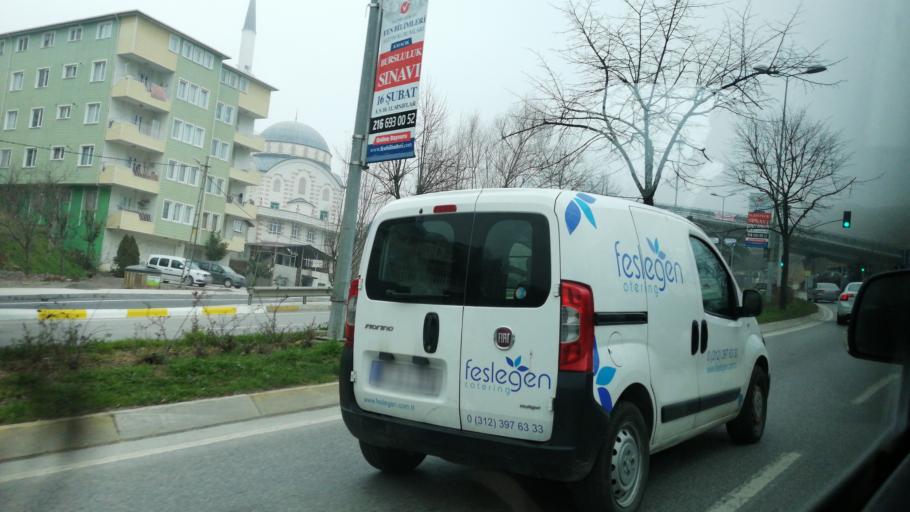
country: TR
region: Istanbul
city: Umraniye
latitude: 41.0845
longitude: 29.0853
